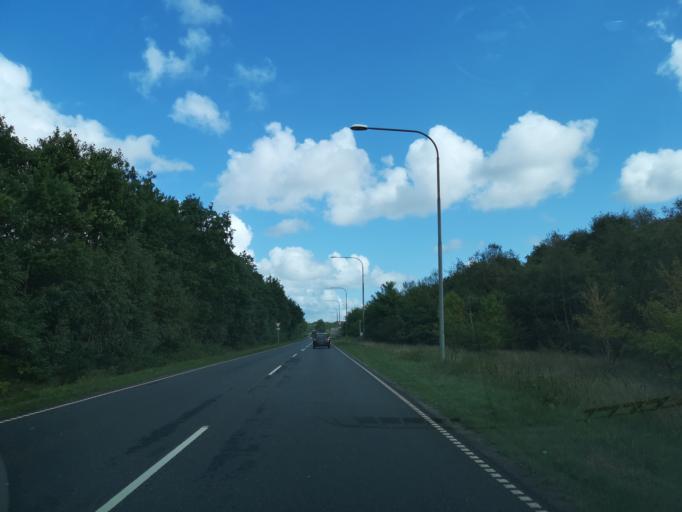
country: DK
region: Central Jutland
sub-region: Holstebro Kommune
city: Holstebro
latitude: 56.3716
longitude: 8.5855
